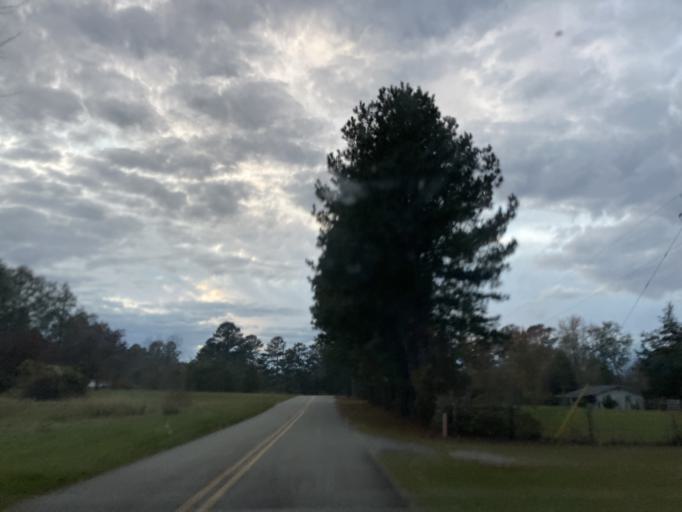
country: US
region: Georgia
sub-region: Jones County
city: Gray
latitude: 32.9769
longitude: -83.5159
